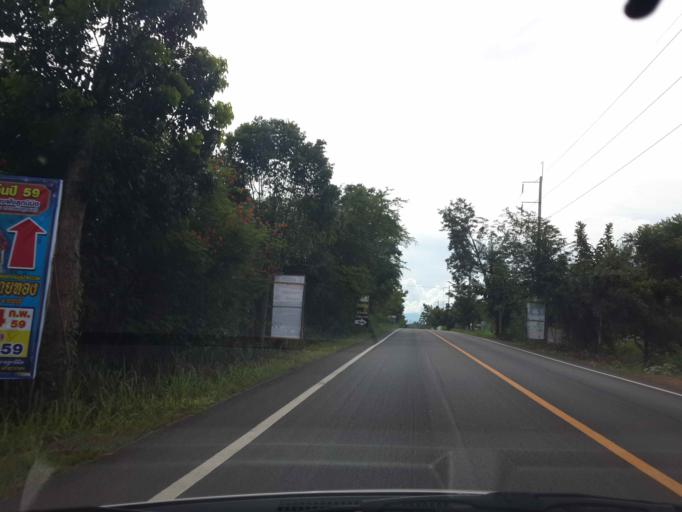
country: TH
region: Ratchaburi
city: Suan Phueng
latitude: 13.5481
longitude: 99.4684
